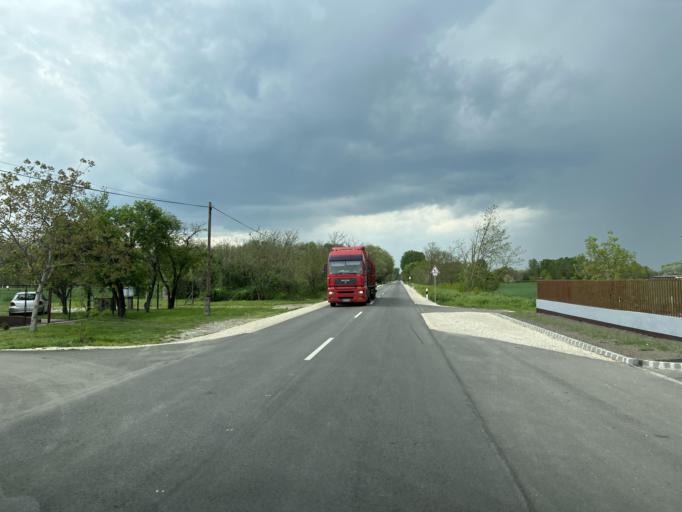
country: HU
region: Pest
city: Nagykoros
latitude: 47.0406
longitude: 19.7467
